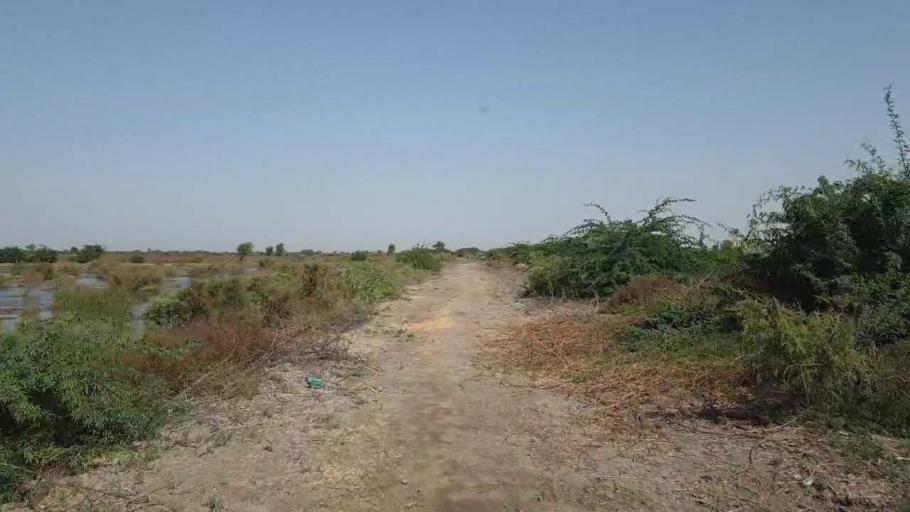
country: PK
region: Sindh
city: Tando Bago
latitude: 24.7164
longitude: 69.0723
